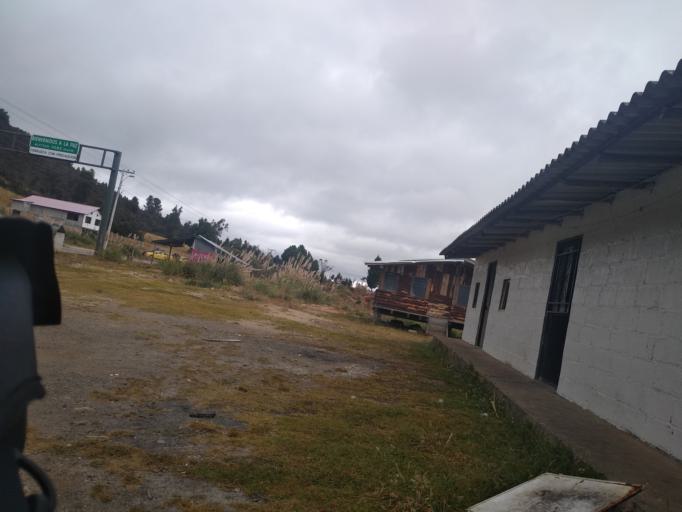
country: EC
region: Azuay
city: Cuenca
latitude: -3.3172
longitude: -79.1538
